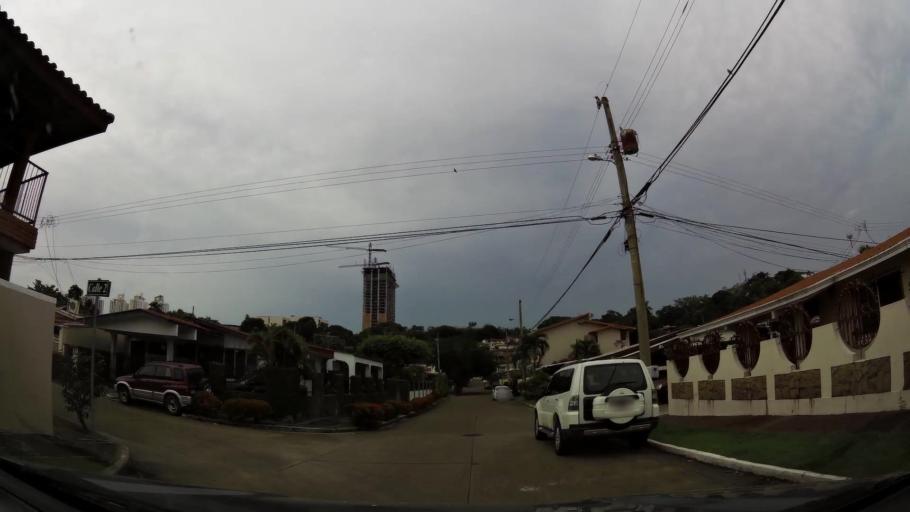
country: PA
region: Panama
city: Panama
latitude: 9.0230
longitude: -79.5171
